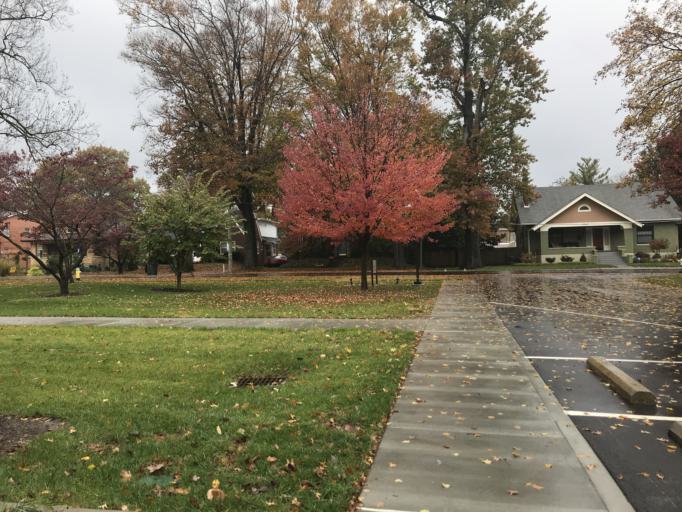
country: US
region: Kentucky
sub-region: Jefferson County
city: Saint Matthews
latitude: 38.2496
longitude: -85.6495
